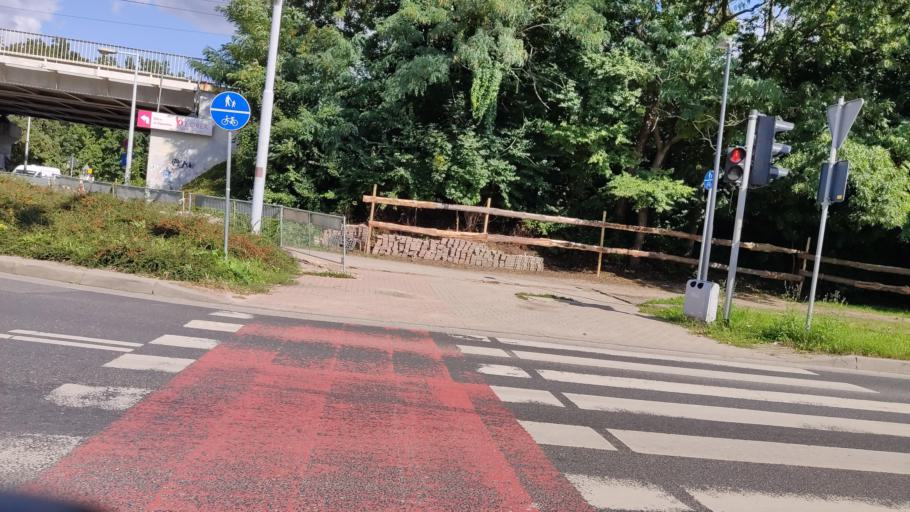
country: PL
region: Lower Silesian Voivodeship
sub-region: Powiat wroclawski
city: Wroclaw
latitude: 51.0809
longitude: 16.9990
